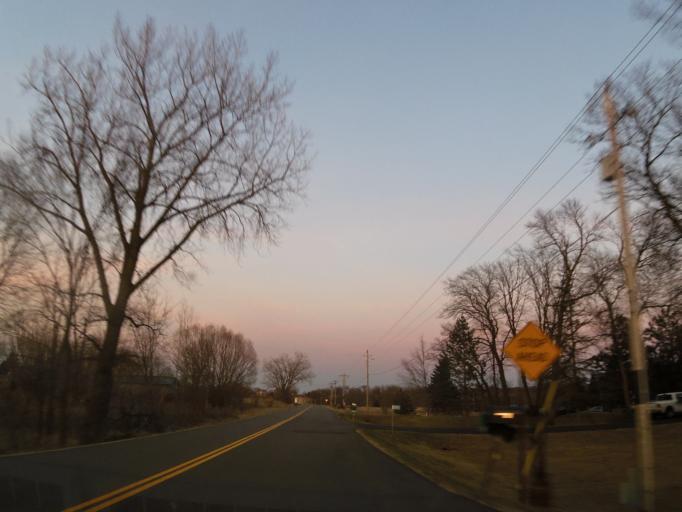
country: US
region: Minnesota
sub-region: Scott County
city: Prior Lake
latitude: 44.6885
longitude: -93.4633
